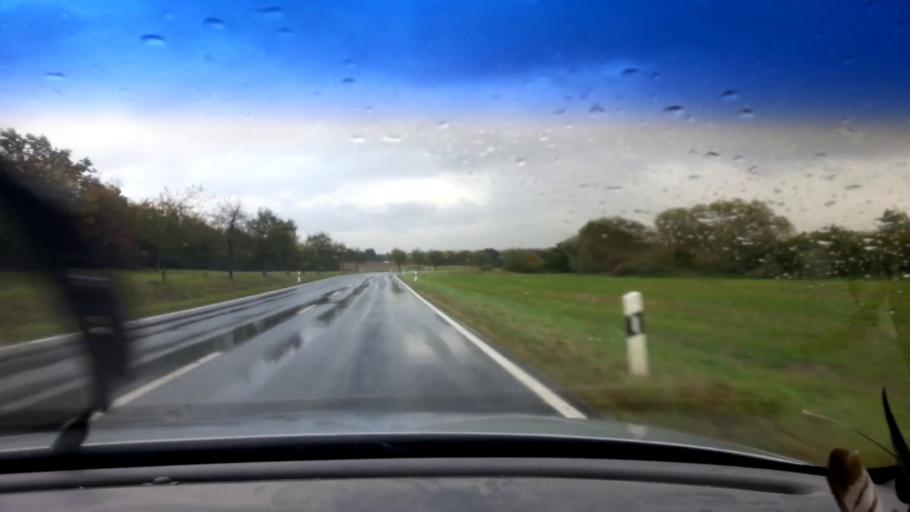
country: DE
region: Bavaria
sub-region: Upper Franconia
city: Burgebrach
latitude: 49.8371
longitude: 10.7368
